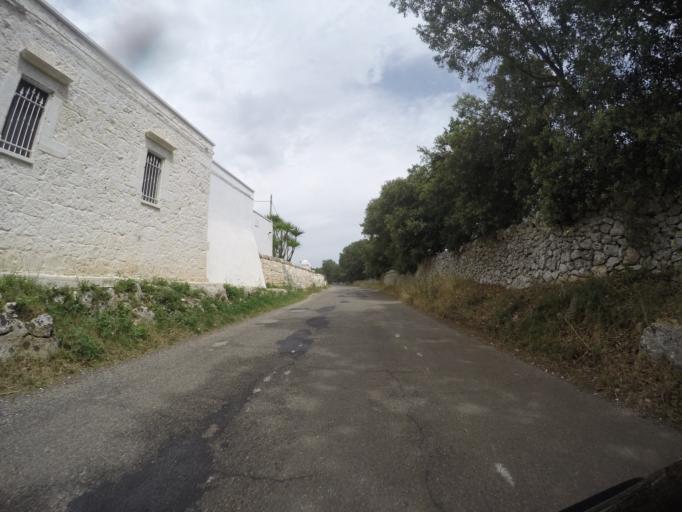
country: IT
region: Apulia
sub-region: Provincia di Taranto
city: Martina Franca
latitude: 40.6652
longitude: 17.3474
